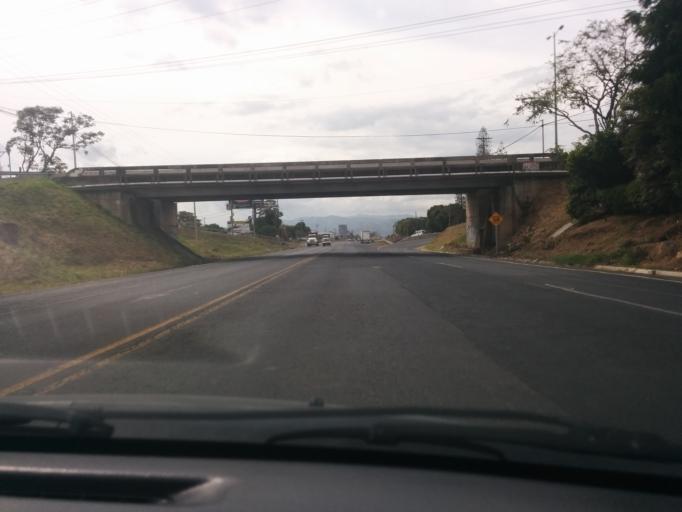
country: CR
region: Alajuela
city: Carrillos
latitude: 9.9966
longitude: -84.2683
